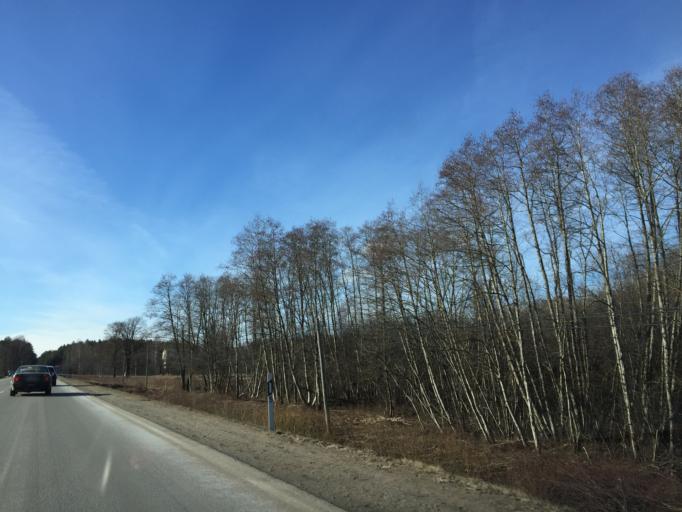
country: LV
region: Stopini
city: Ulbroka
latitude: 56.9451
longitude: 24.3707
